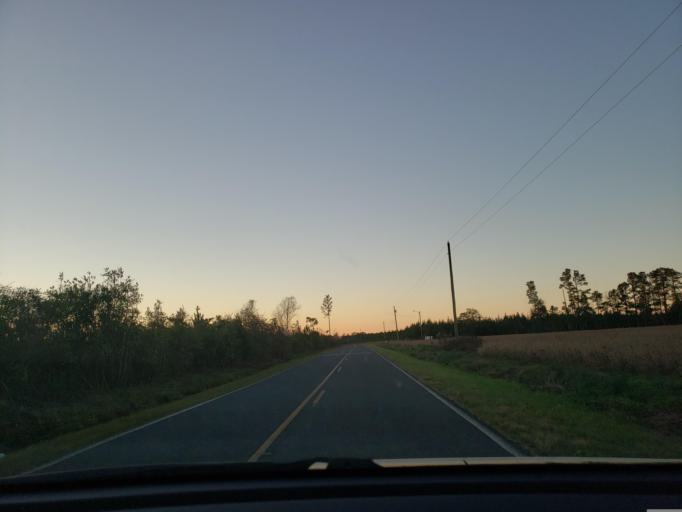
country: US
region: North Carolina
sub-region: Onslow County
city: Richlands
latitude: 34.7359
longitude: -77.6223
